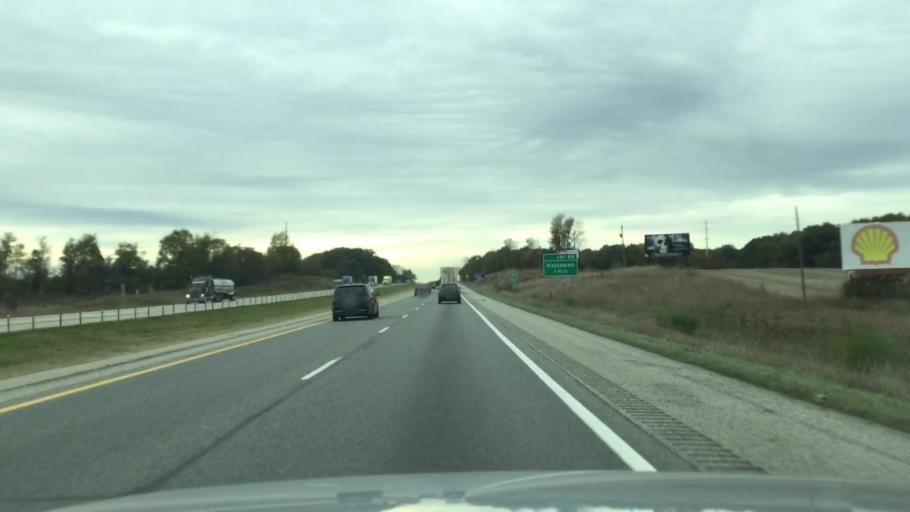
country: US
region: Michigan
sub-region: Van Buren County
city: Mattawan
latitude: 42.2233
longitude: -85.7577
